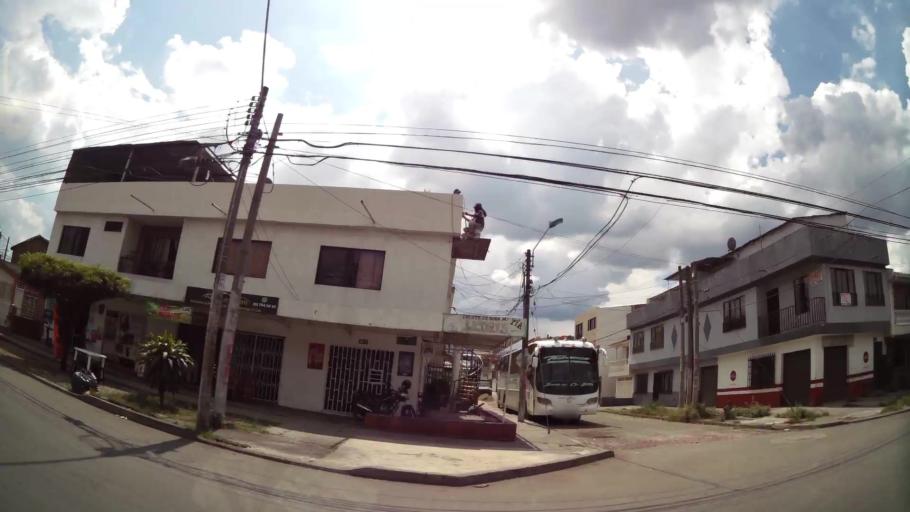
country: CO
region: Valle del Cauca
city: Cali
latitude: 3.4695
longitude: -76.5046
